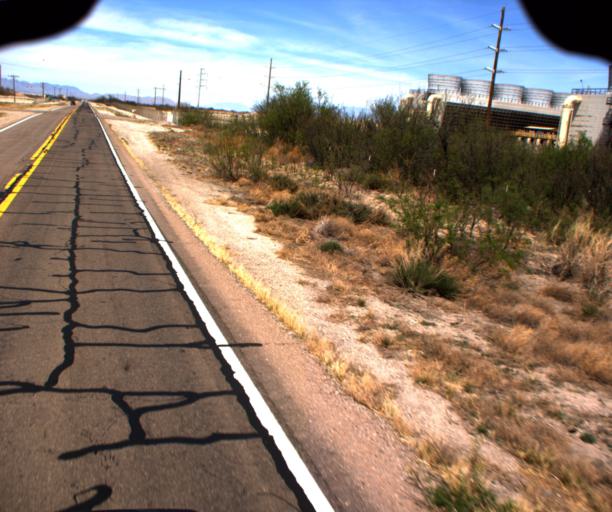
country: US
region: Arizona
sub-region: Cochise County
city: Willcox
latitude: 32.0606
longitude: -109.8913
